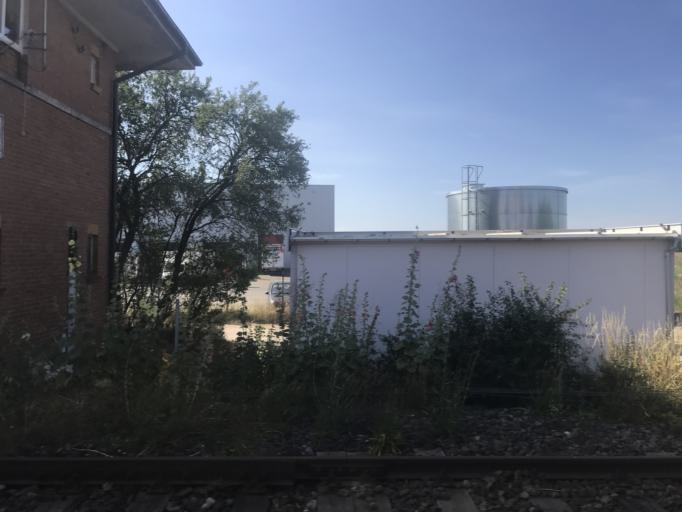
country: PL
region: West Pomeranian Voivodeship
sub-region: Powiat policki
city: Przeclaw
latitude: 53.3942
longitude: 14.4798
